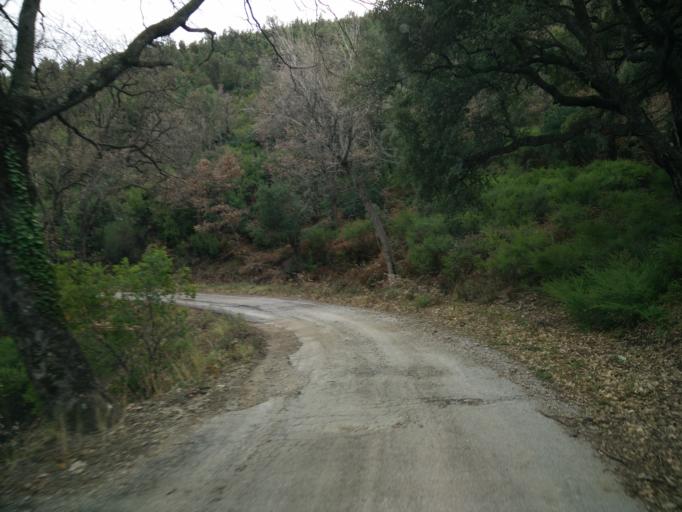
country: FR
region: Provence-Alpes-Cote d'Azur
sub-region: Departement du Var
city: Roquebrune-sur-Argens
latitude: 43.3932
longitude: 6.6089
